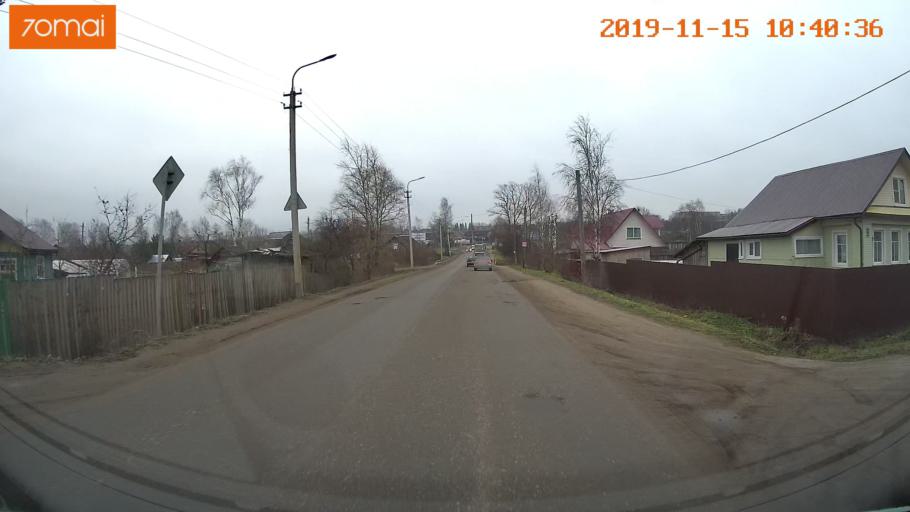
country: RU
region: Vologda
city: Sheksna
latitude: 59.2131
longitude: 38.5097
